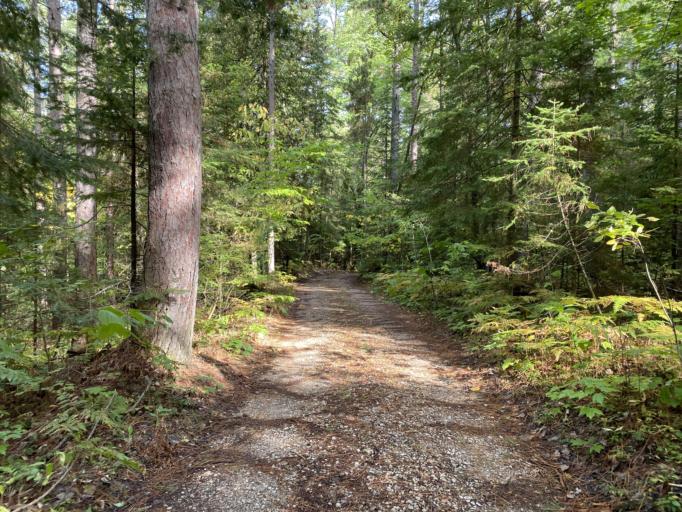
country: US
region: Michigan
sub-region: Mackinac County
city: Saint Ignace
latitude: 45.7480
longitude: -84.8795
